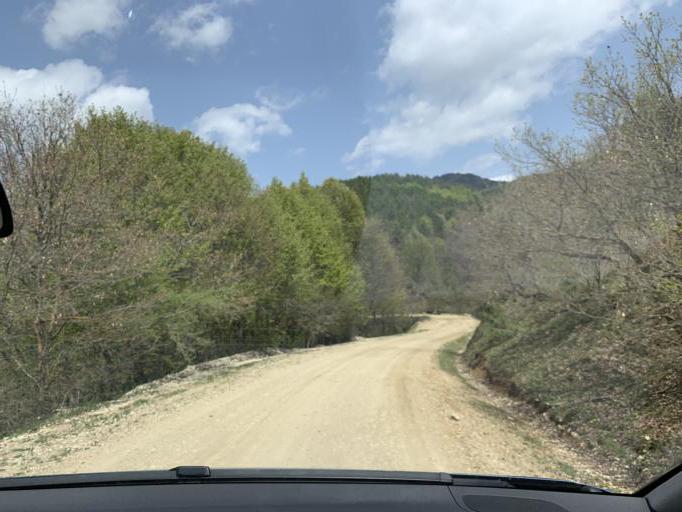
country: TR
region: Bolu
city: Bolu
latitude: 40.8319
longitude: 31.6738
